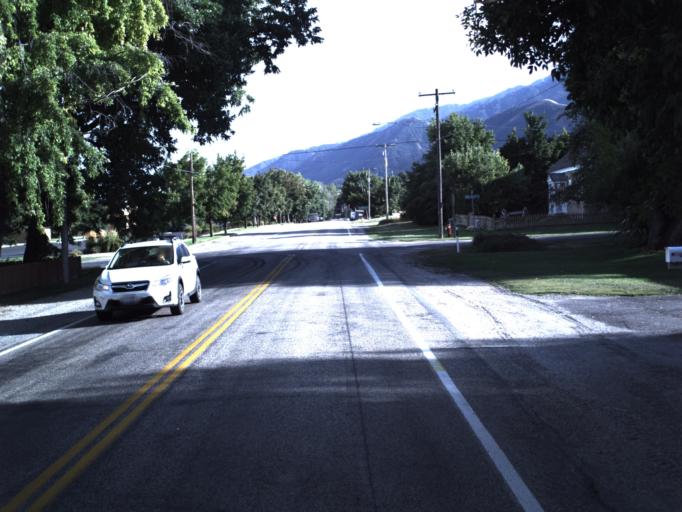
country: US
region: Utah
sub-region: Cache County
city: Mendon
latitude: 41.7105
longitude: -111.9792
